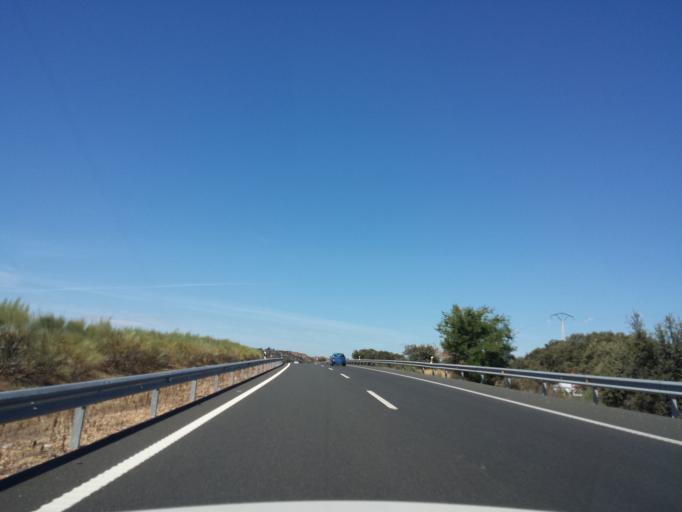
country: ES
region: Extremadura
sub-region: Provincia de Caceres
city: Peraleda de la Mata
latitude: 39.8891
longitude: -5.4830
